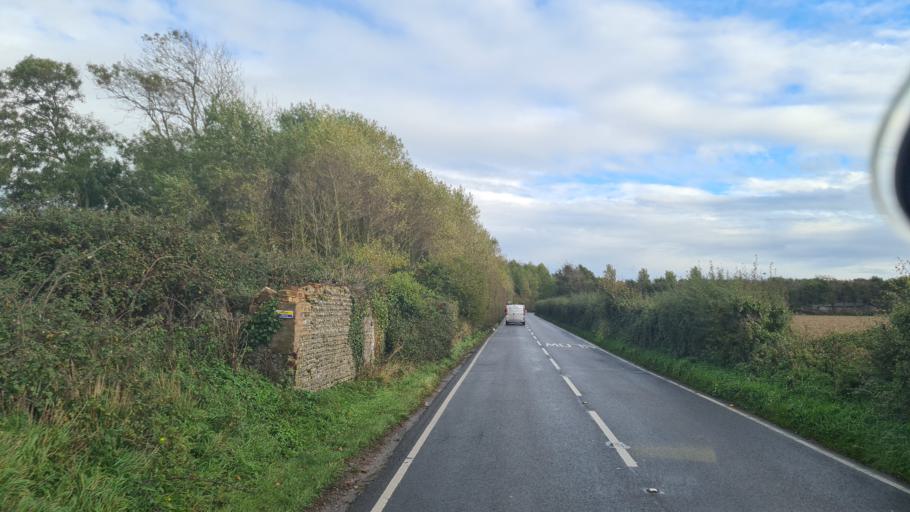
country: GB
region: England
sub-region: West Sussex
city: Walberton
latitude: 50.8092
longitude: -0.5884
